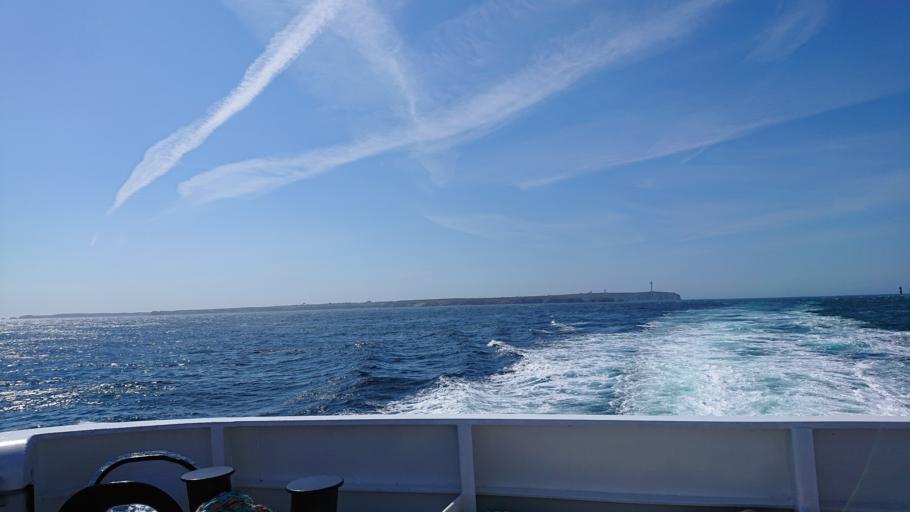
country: FR
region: Brittany
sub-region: Departement du Finistere
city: Porspoder
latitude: 48.4514
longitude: -5.0078
